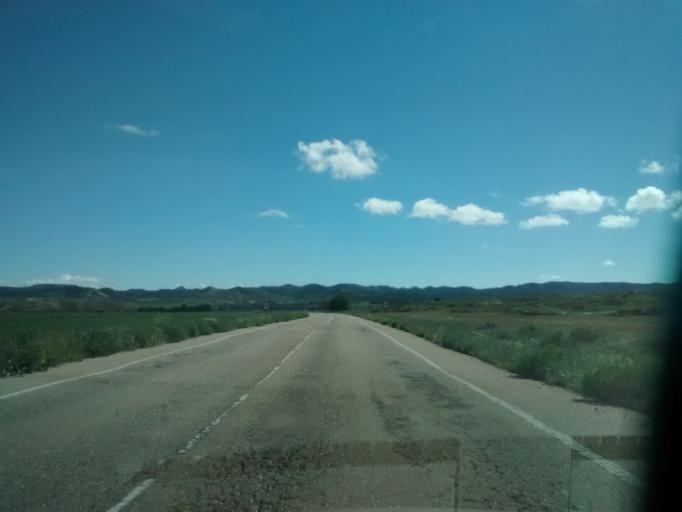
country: ES
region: Aragon
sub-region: Provincia de Zaragoza
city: Lecinena
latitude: 41.8084
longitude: -0.5872
